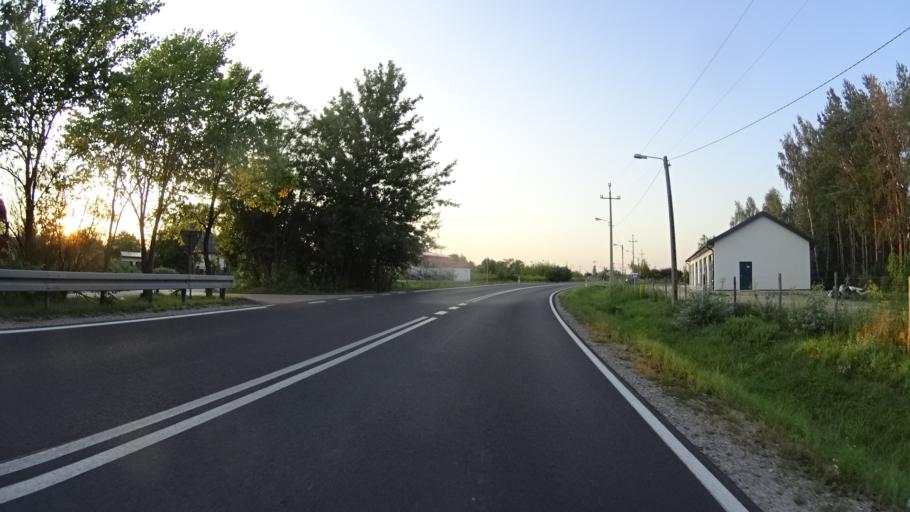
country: PL
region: Masovian Voivodeship
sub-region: Powiat warszawski zachodni
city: Truskaw
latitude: 52.2498
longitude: 20.7415
